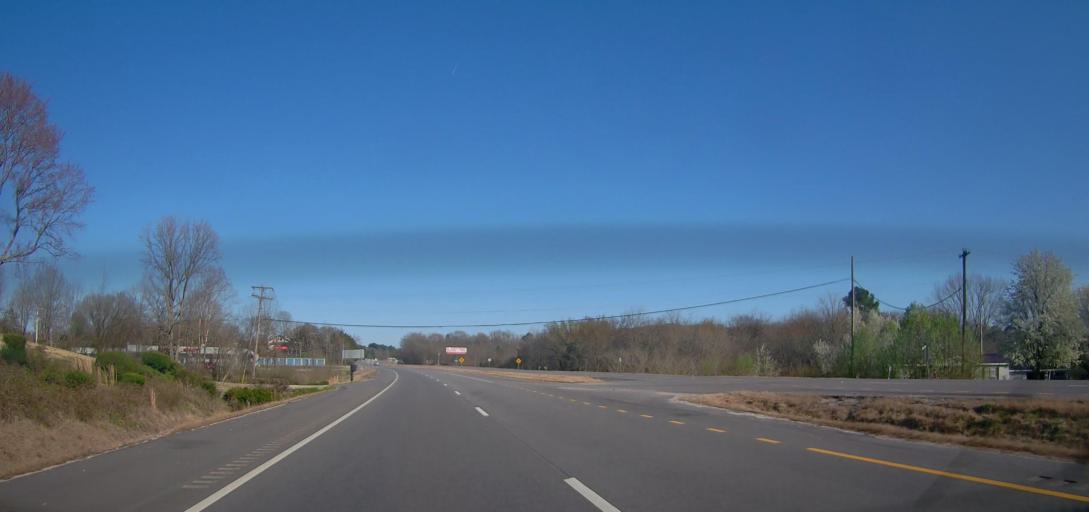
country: US
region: Alabama
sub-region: Colbert County
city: Cherokee
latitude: 34.7554
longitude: -87.9781
